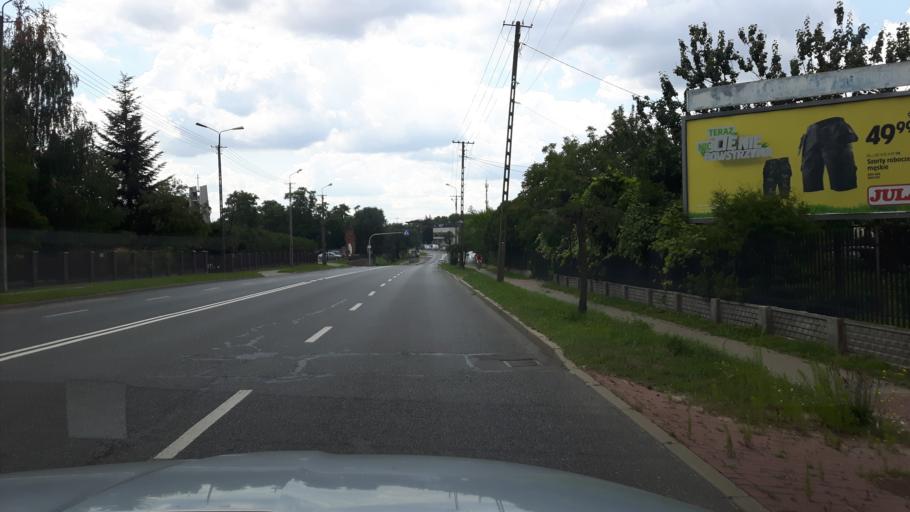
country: PL
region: Masovian Voivodeship
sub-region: Powiat wyszkowski
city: Wyszkow
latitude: 52.5957
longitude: 21.4608
